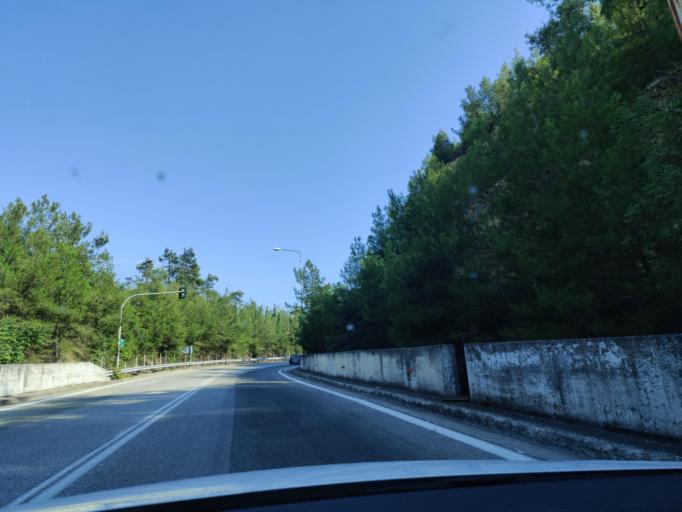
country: GR
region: East Macedonia and Thrace
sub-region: Nomos Kavalas
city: Amygdaleonas
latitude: 40.9426
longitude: 24.3739
